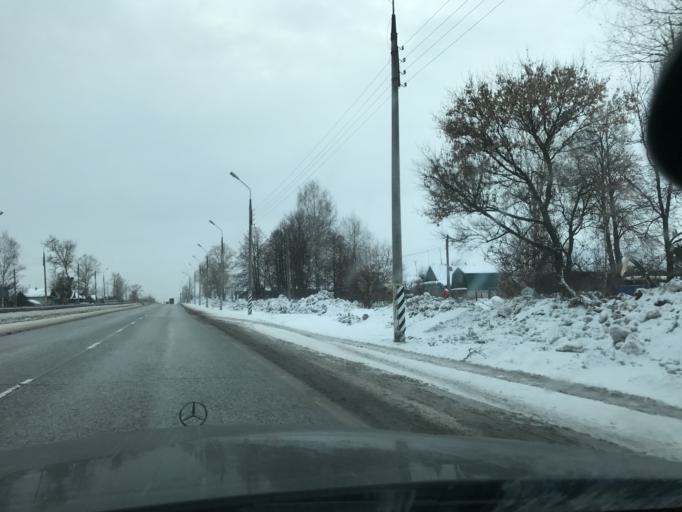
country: RU
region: Nizjnij Novgorod
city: Mulino
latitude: 56.2716
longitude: 42.9557
